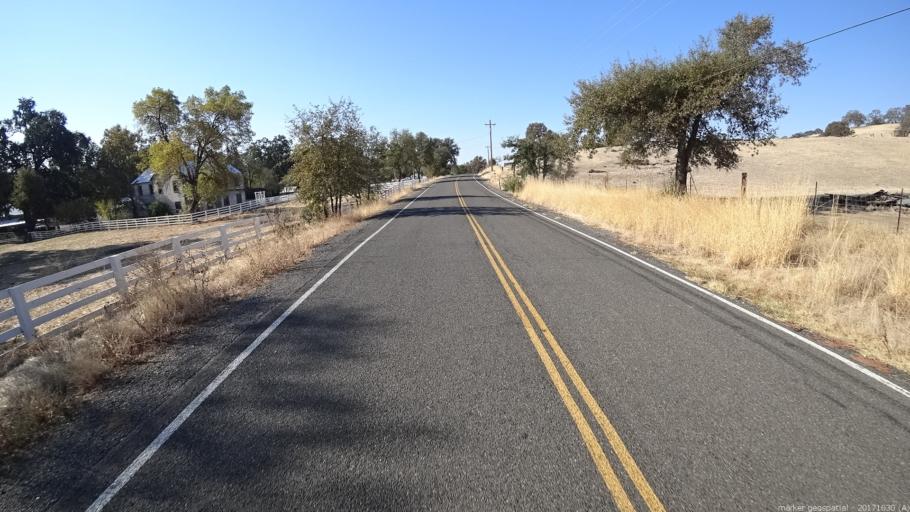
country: US
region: California
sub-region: Shasta County
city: Bella Vista
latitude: 40.6223
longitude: -122.1121
